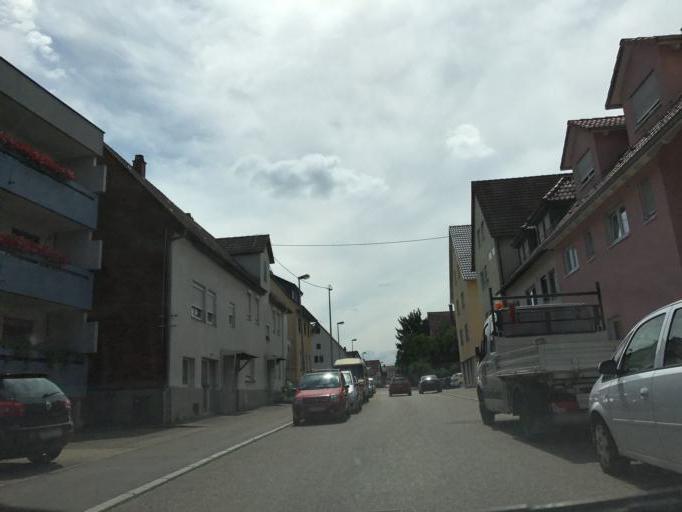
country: DE
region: Baden-Wuerttemberg
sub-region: Regierungsbezirk Stuttgart
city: Waiblingen
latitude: 48.8050
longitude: 9.3224
